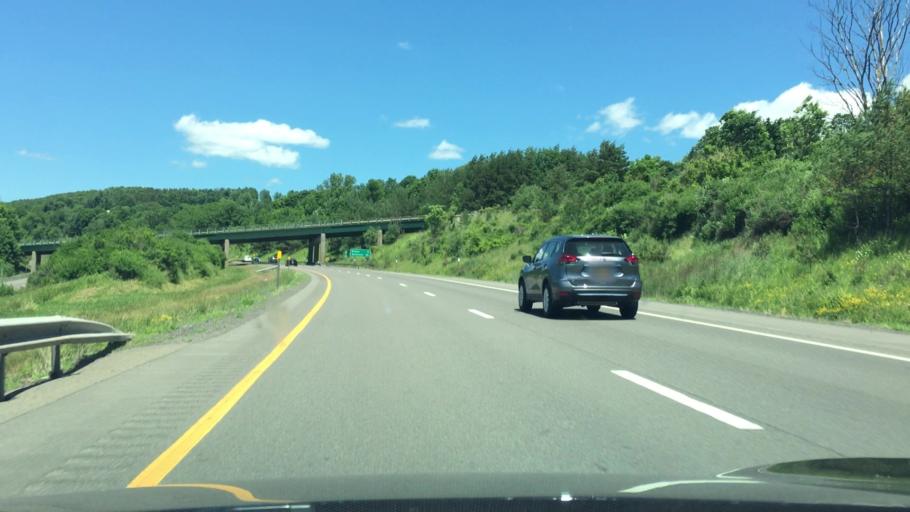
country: US
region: New York
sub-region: Cortland County
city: Homer
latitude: 42.6284
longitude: -76.1742
